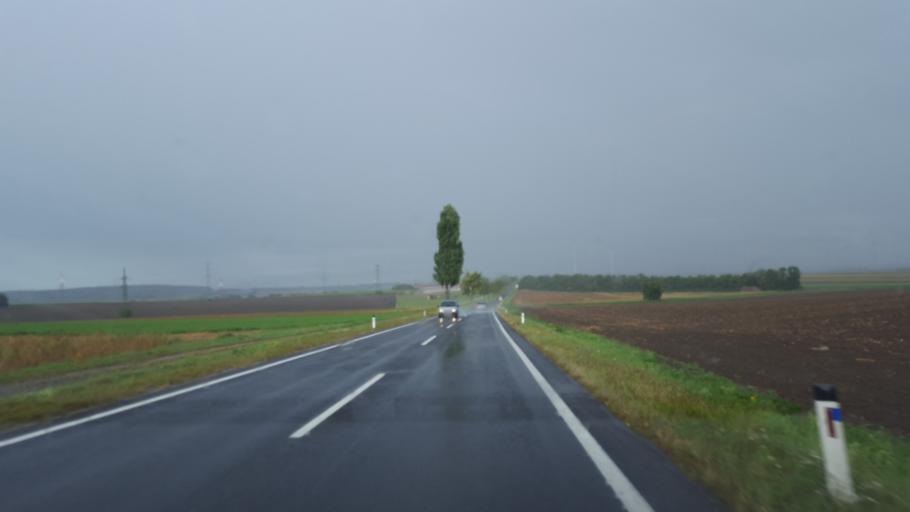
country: AT
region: Lower Austria
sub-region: Politischer Bezirk Bruck an der Leitha
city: Bruck an der Leitha
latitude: 48.0340
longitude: 16.7438
